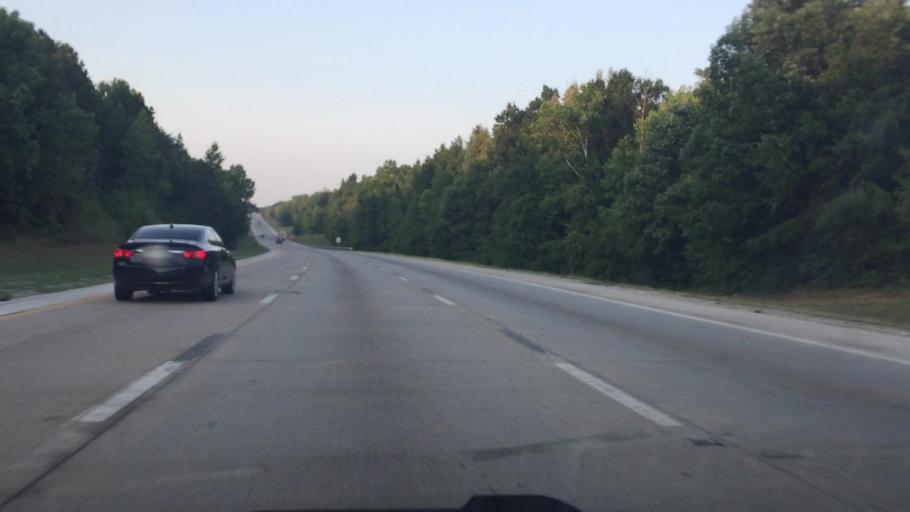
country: US
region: North Carolina
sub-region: Guilford County
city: Jamestown
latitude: 35.9781
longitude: -79.8902
